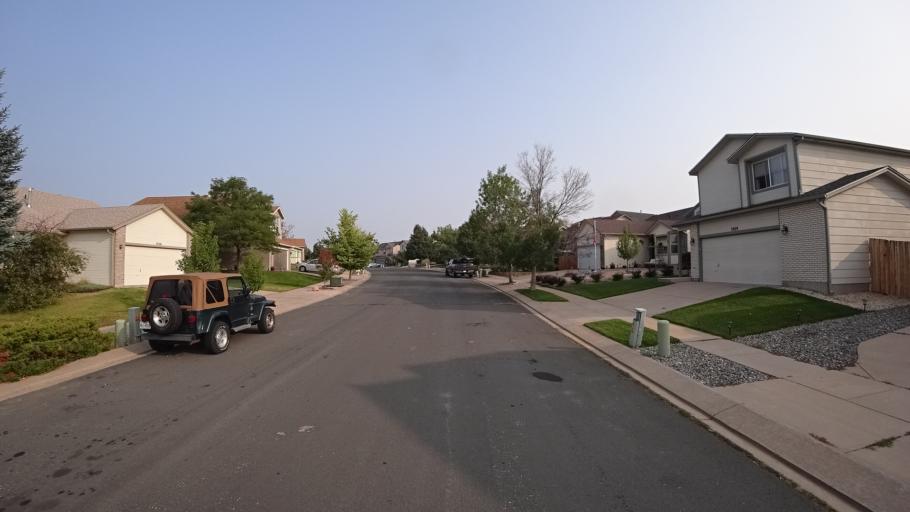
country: US
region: Colorado
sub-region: El Paso County
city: Cimarron Hills
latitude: 38.9350
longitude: -104.7246
